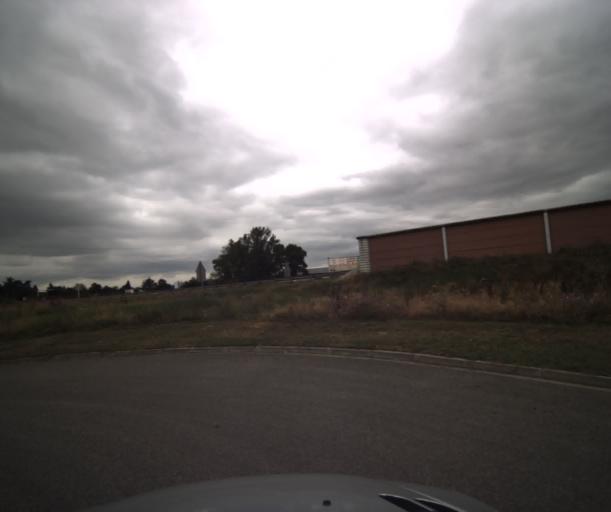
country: FR
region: Midi-Pyrenees
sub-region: Departement de la Haute-Garonne
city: Lacroix-Falgarde
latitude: 43.4933
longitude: 1.3961
